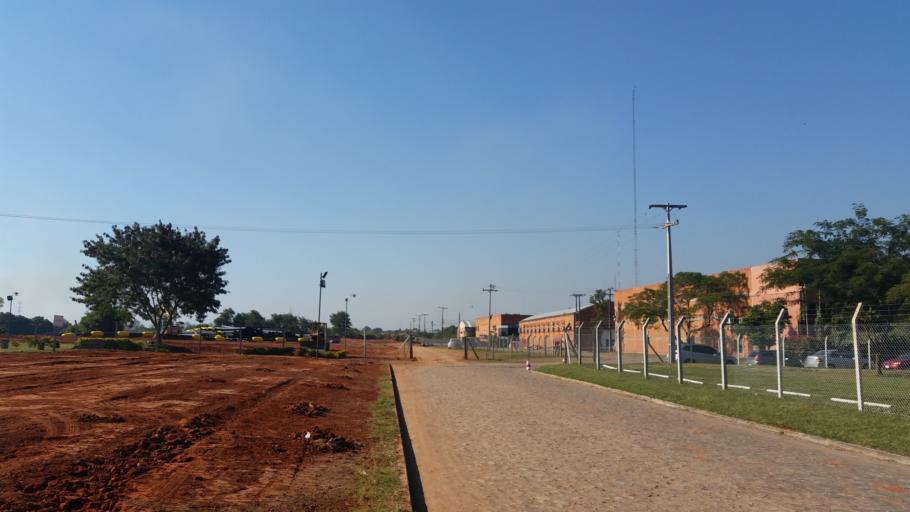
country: PY
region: Asuncion
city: Asuncion
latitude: -25.2712
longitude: -57.6093
